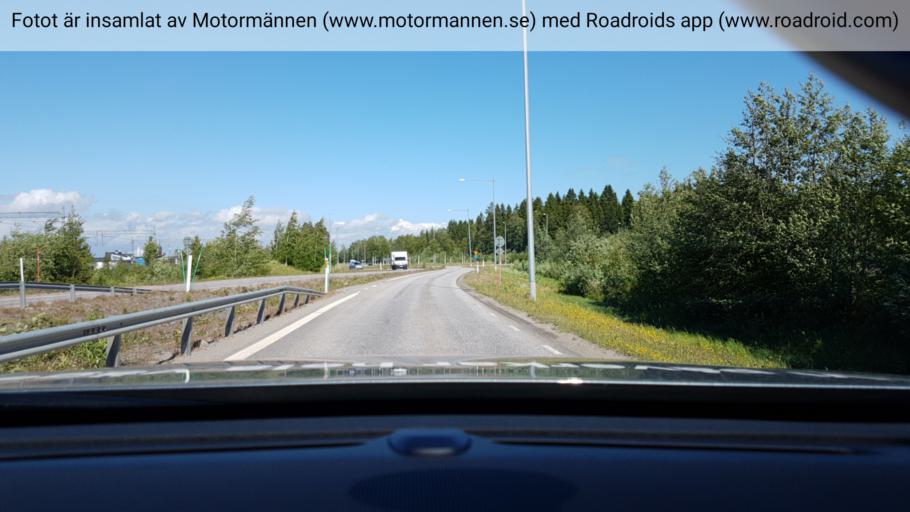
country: SE
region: Vaesterbotten
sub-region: Umea Kommun
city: Umea
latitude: 63.7908
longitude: 20.3133
